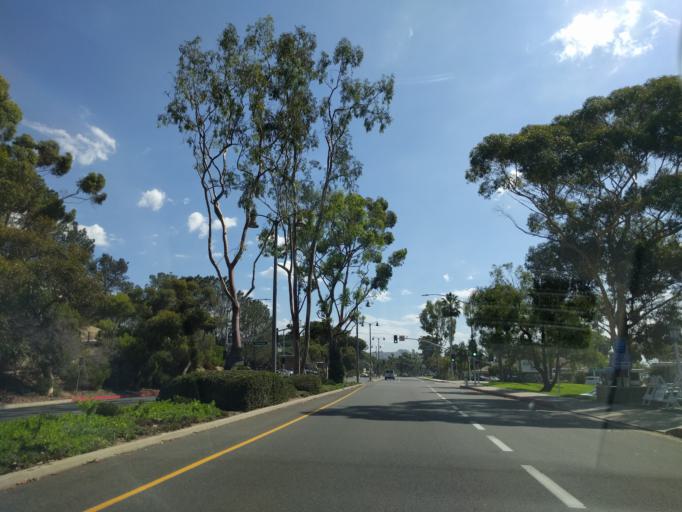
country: US
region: California
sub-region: Orange County
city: Dana Point
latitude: 33.4623
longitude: -117.6966
